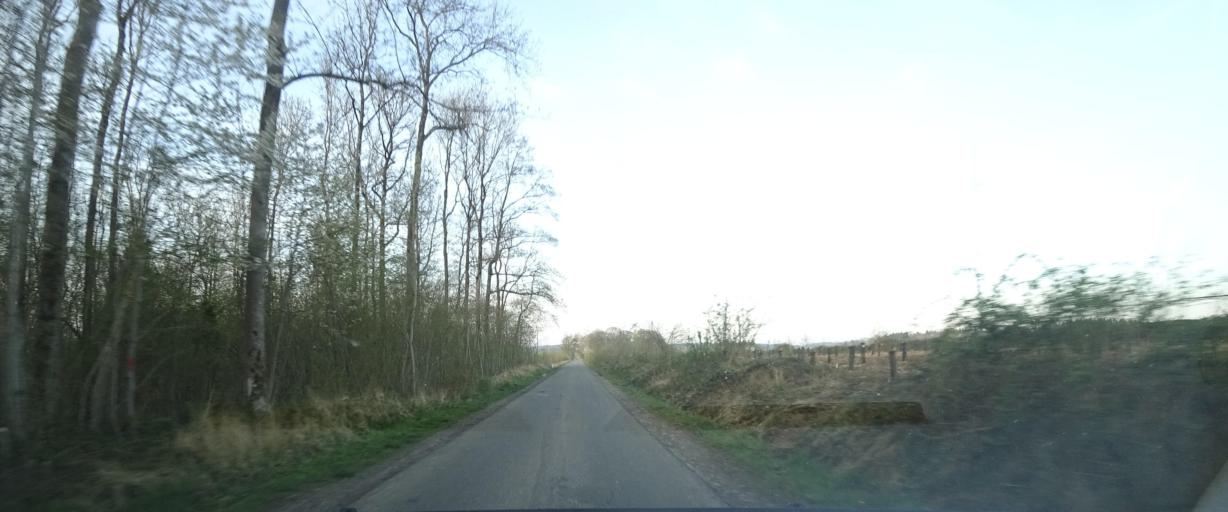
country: BE
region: Wallonia
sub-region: Province de Namur
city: Hamois
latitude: 50.3102
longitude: 5.1772
